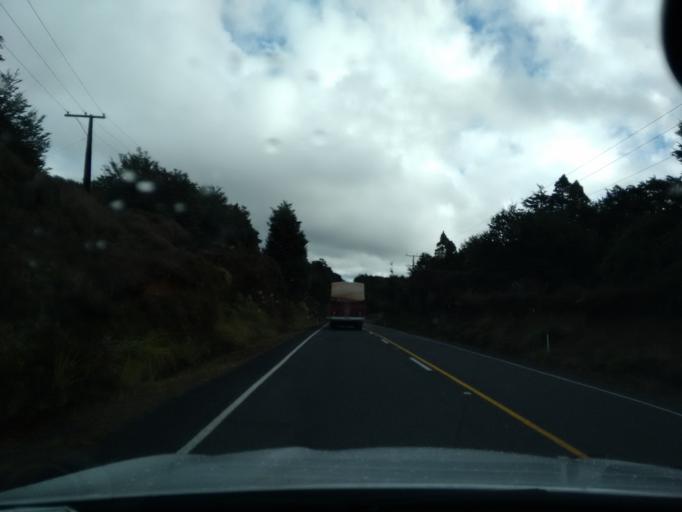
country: NZ
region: Manawatu-Wanganui
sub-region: Ruapehu District
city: Waiouru
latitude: -39.1738
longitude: 175.4741
